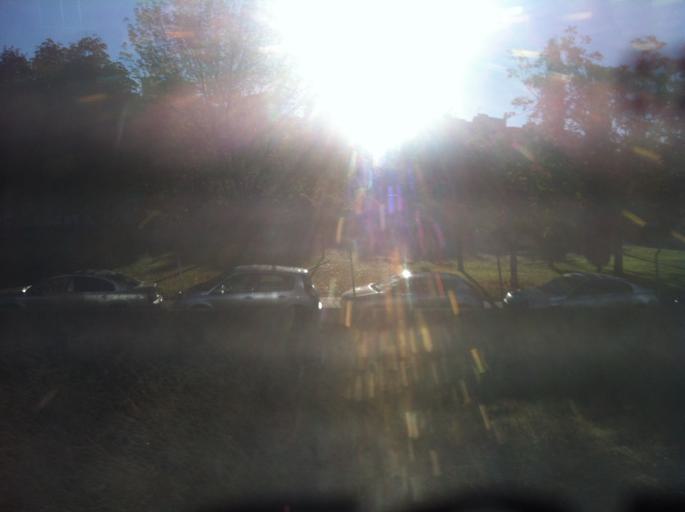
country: ES
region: Castille and Leon
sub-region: Provincia de Valladolid
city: Valladolid
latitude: 41.6544
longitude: -4.7078
